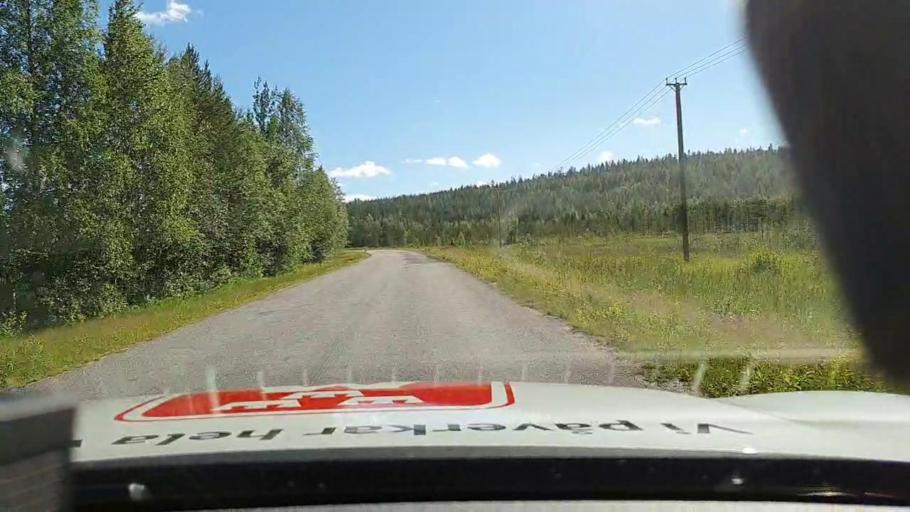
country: SE
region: Norrbotten
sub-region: Overkalix Kommun
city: OEverkalix
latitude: 66.2466
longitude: 23.0051
